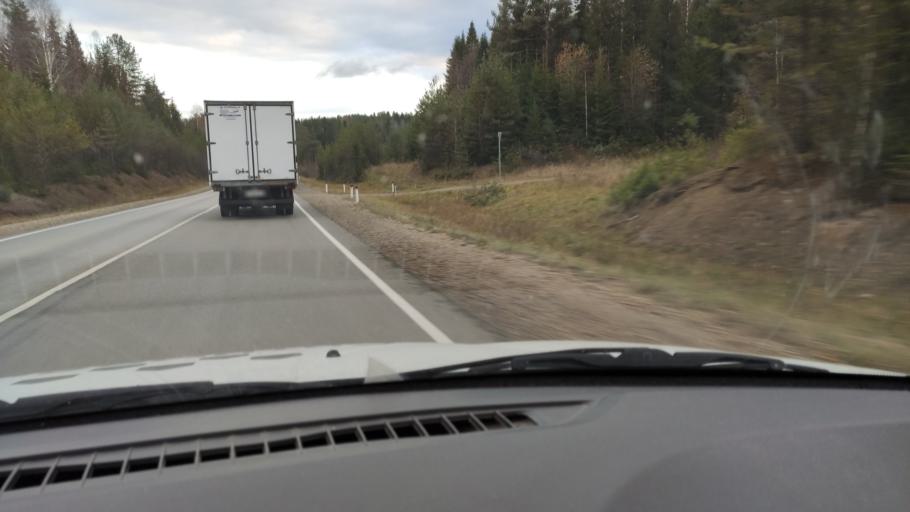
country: RU
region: Kirov
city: Chernaya Kholunitsa
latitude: 58.8499
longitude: 51.7415
